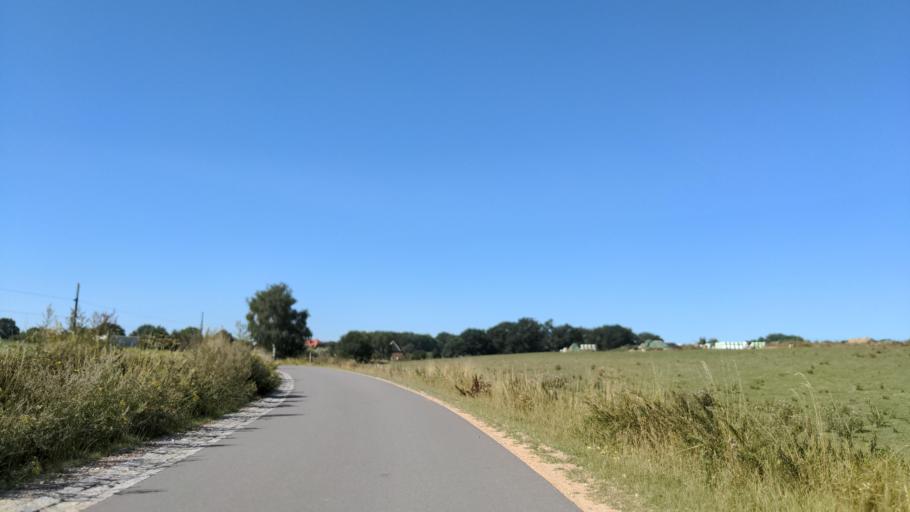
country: DE
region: Mecklenburg-Vorpommern
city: Selmsdorf
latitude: 53.8377
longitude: 10.8748
